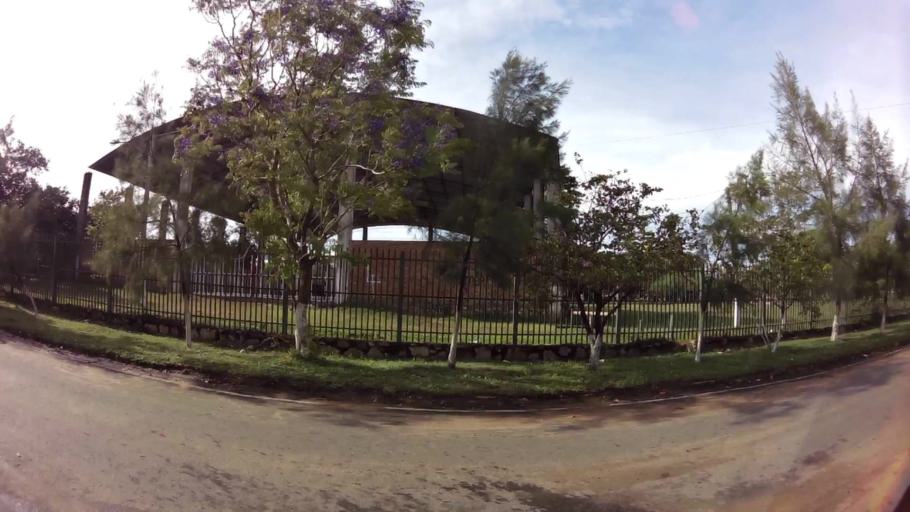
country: PY
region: Central
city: Limpio
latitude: -25.1670
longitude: -57.4794
